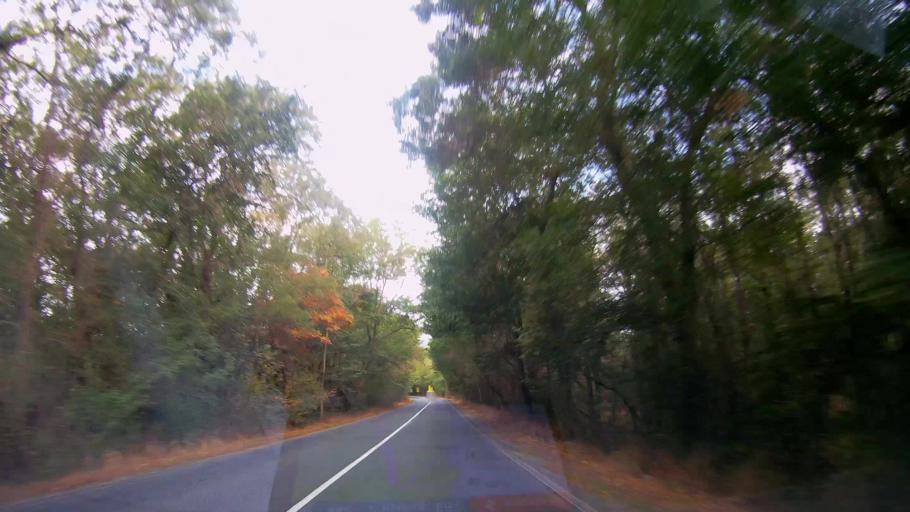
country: BG
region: Burgas
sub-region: Obshtina Primorsko
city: Primorsko
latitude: 42.3025
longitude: 27.7261
